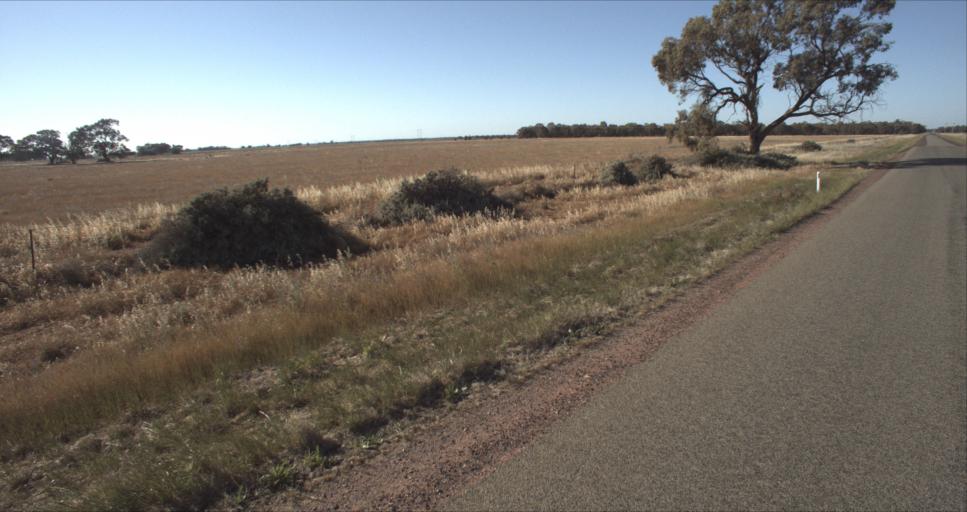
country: AU
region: New South Wales
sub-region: Leeton
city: Leeton
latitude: -34.5561
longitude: 146.2663
